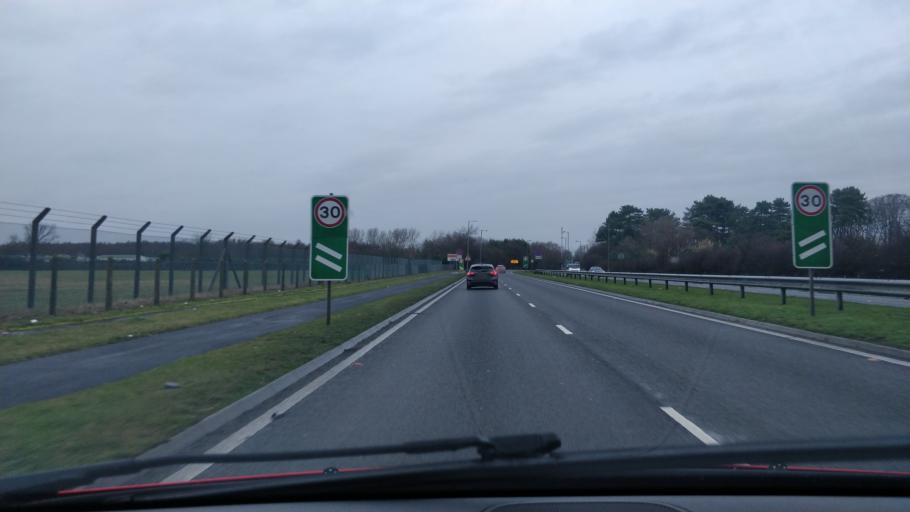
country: GB
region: England
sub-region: Sefton
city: Formby
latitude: 53.5847
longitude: -3.0446
